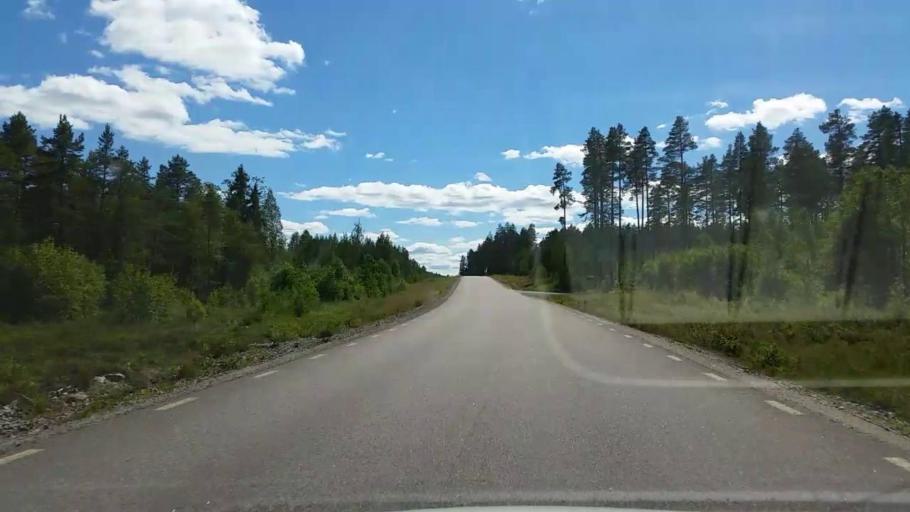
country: SE
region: Dalarna
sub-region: Faluns Kommun
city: Svardsjo
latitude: 61.0273
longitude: 15.7610
